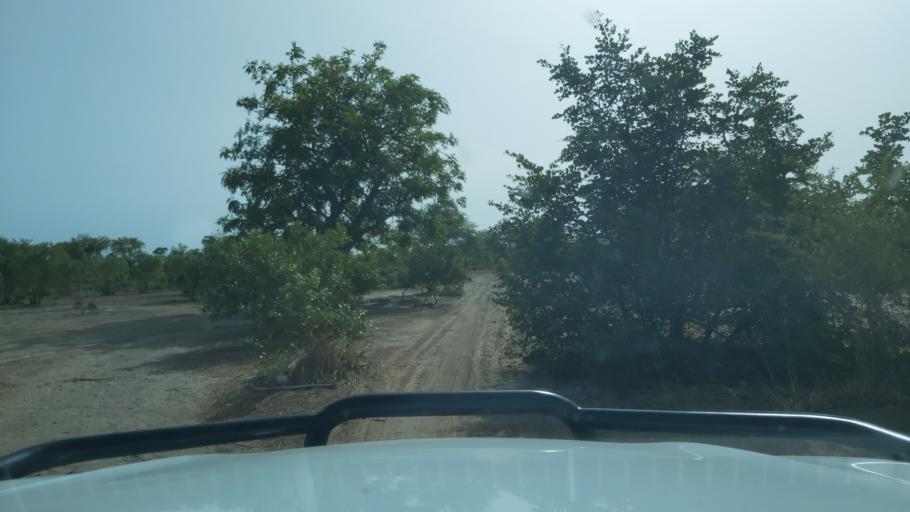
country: ML
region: Koulikoro
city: Koulikoro
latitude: 13.1760
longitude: -7.7501
